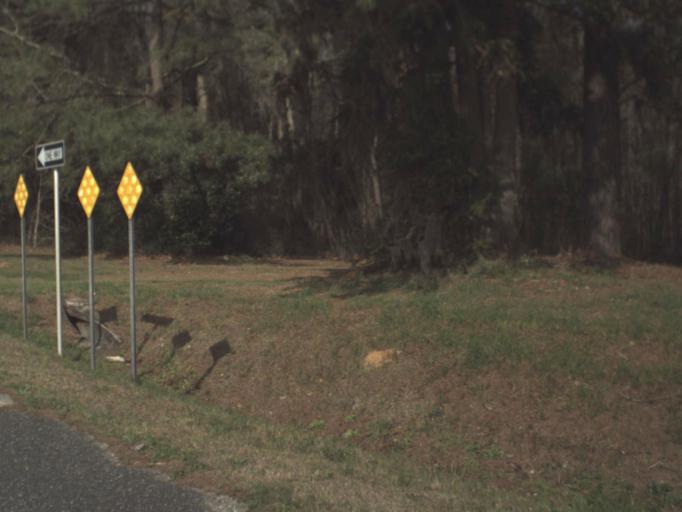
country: US
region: Florida
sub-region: Jefferson County
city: Monticello
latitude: 30.5009
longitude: -83.8790
